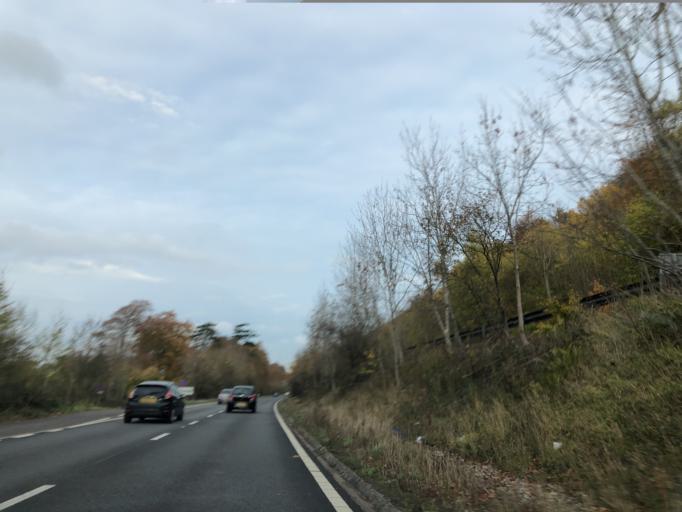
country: GB
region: England
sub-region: Royal Borough of Windsor and Maidenhead
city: Bisham
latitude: 51.5460
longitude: -0.7845
